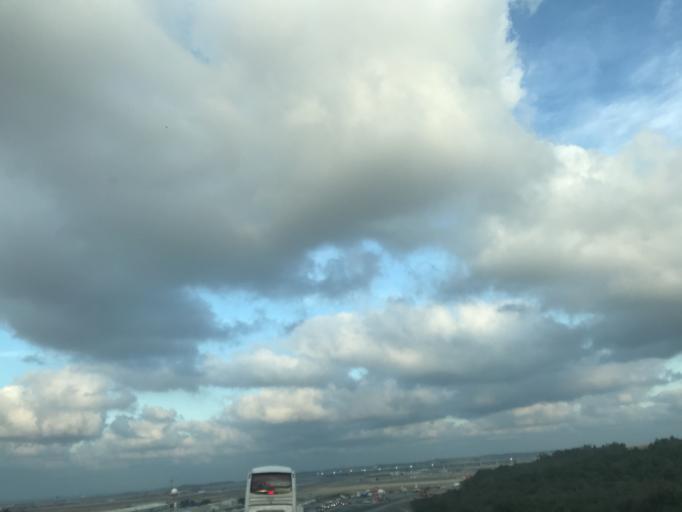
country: TR
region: Istanbul
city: Durusu
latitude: 41.2628
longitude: 28.6945
